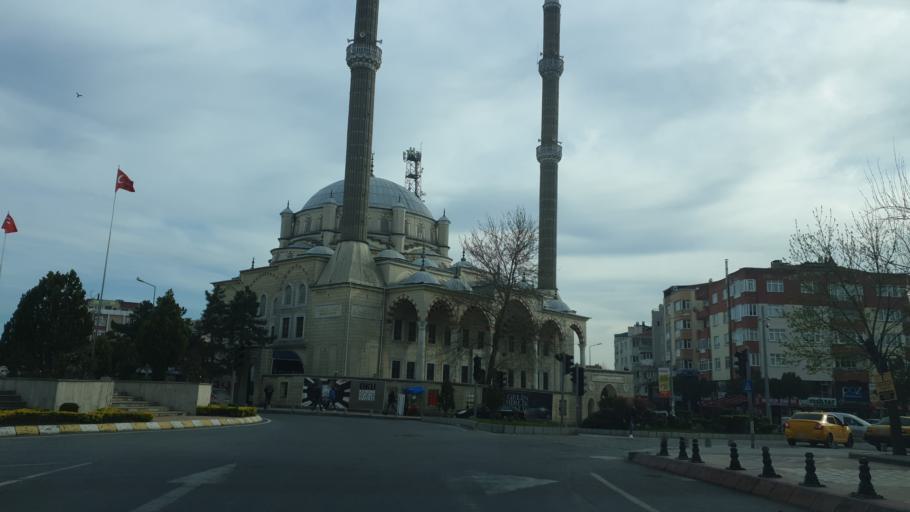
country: TR
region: Tekirdag
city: Cerkezkoey
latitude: 41.2866
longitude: 27.9993
